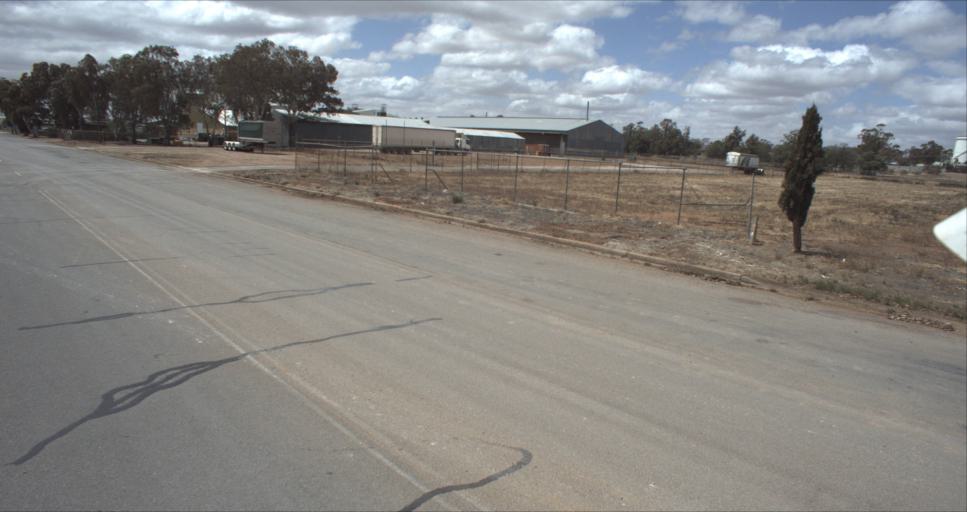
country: AU
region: New South Wales
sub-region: Leeton
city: Leeton
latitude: -34.5582
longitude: 146.3912
